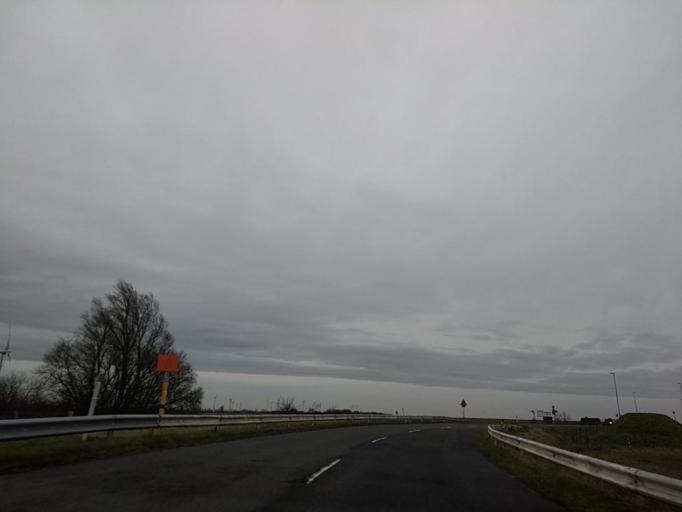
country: NL
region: Groningen
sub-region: Gemeente Delfzijl
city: Delfzijl
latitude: 53.3398
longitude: 7.0222
